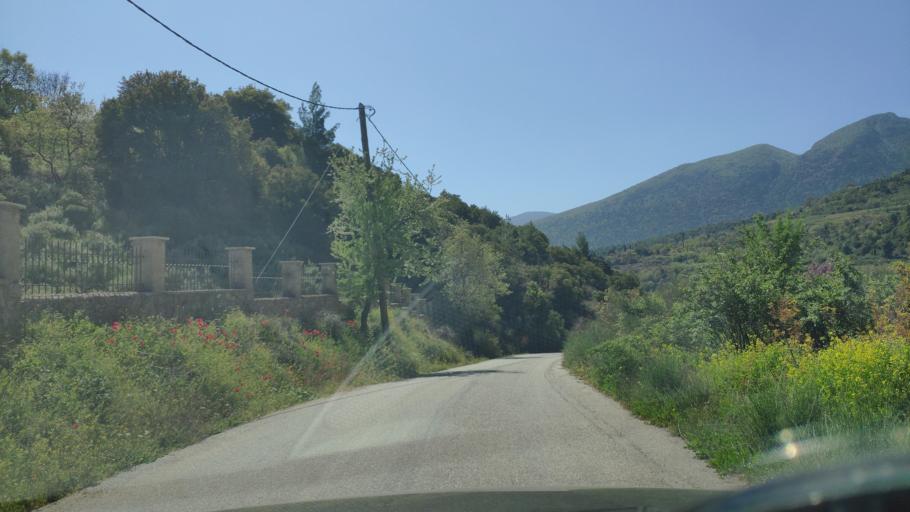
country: GR
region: West Greece
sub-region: Nomos Achaias
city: Akrata
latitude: 38.0941
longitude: 22.3241
